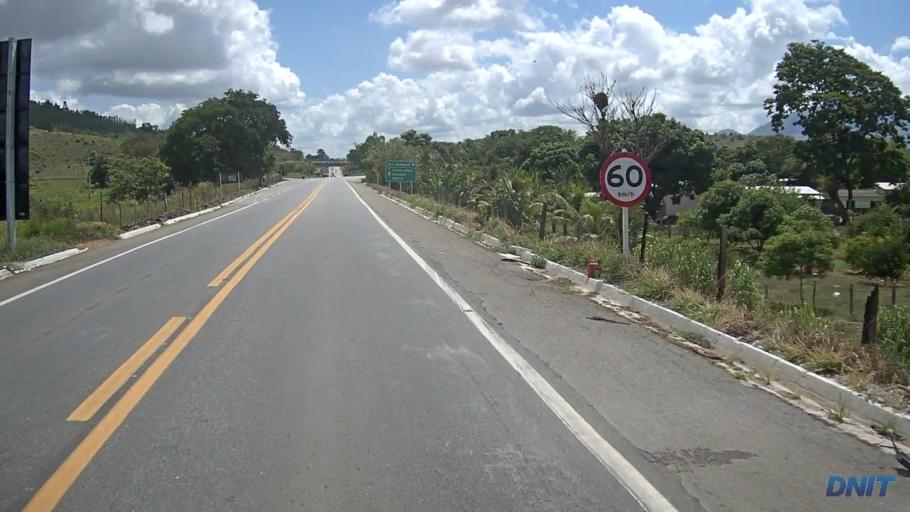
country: BR
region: Minas Gerais
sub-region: Governador Valadares
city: Governador Valadares
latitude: -18.9167
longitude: -42.0124
